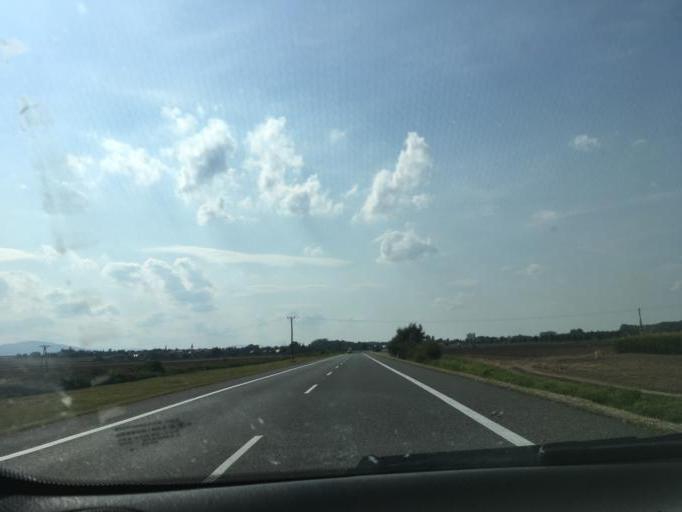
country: PL
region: Opole Voivodeship
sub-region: Powiat prudnicki
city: Lubrza
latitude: 50.3288
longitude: 17.6156
